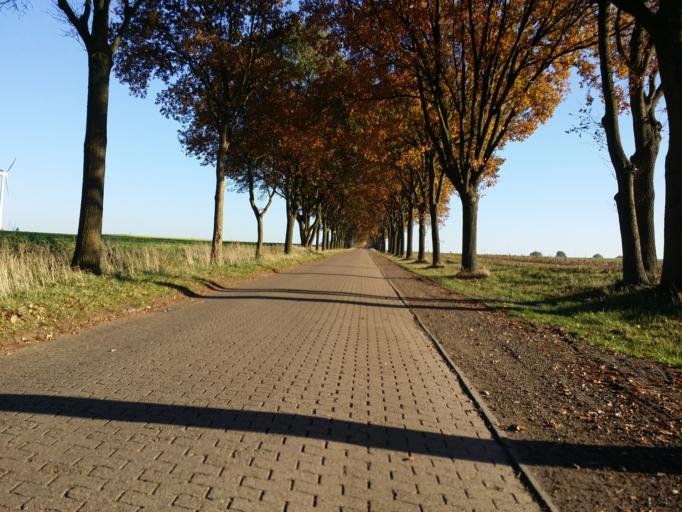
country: DE
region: Lower Saxony
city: Oyten
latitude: 53.0714
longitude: 8.9969
